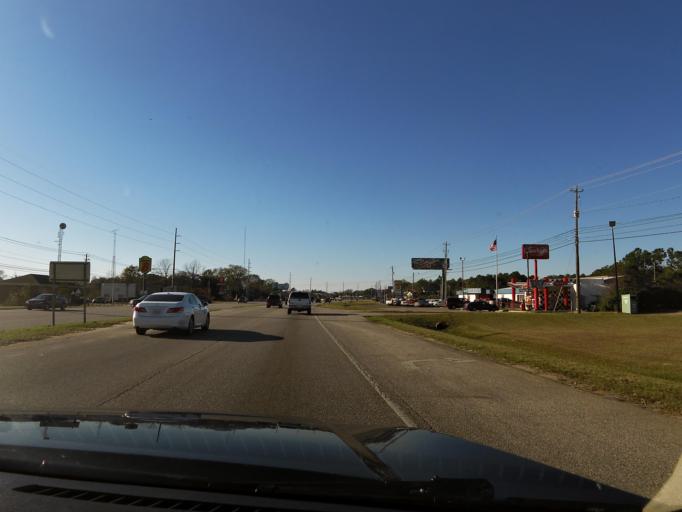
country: US
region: Alabama
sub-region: Houston County
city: Dothan
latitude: 31.1909
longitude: -85.4023
